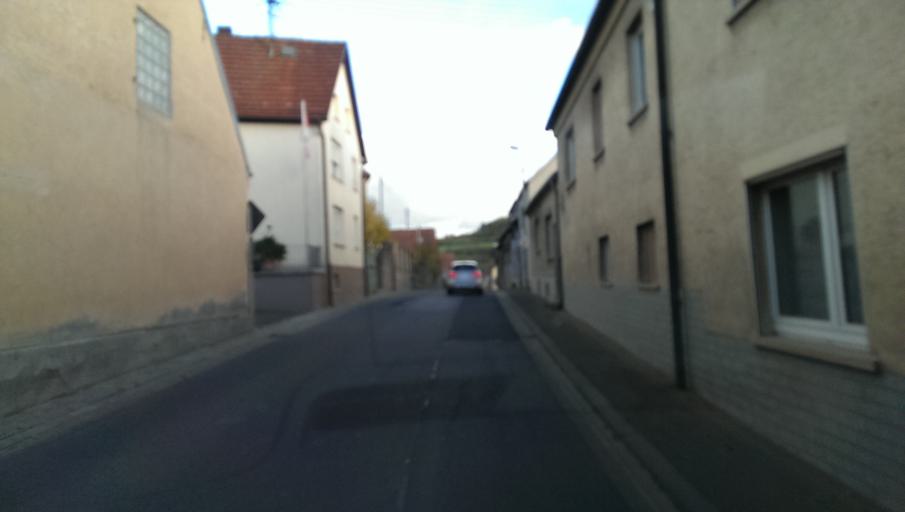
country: DE
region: Bavaria
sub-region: Regierungsbezirk Unterfranken
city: Arnstein
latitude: 49.9687
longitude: 9.9169
